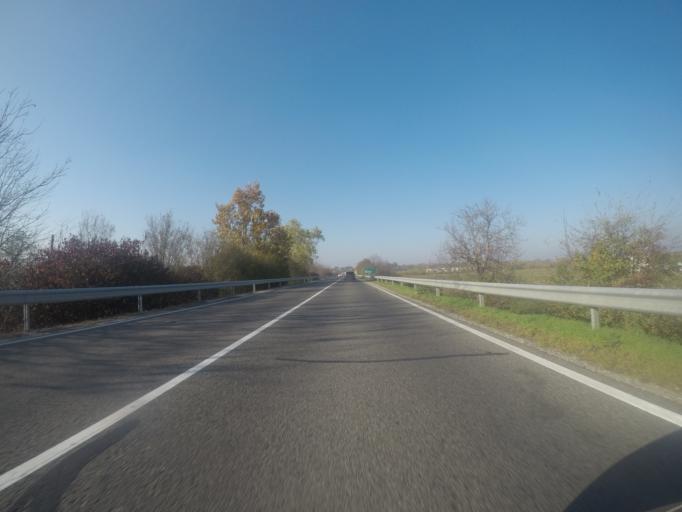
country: HU
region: Fejer
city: Ercsi
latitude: 47.2328
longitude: 18.8922
